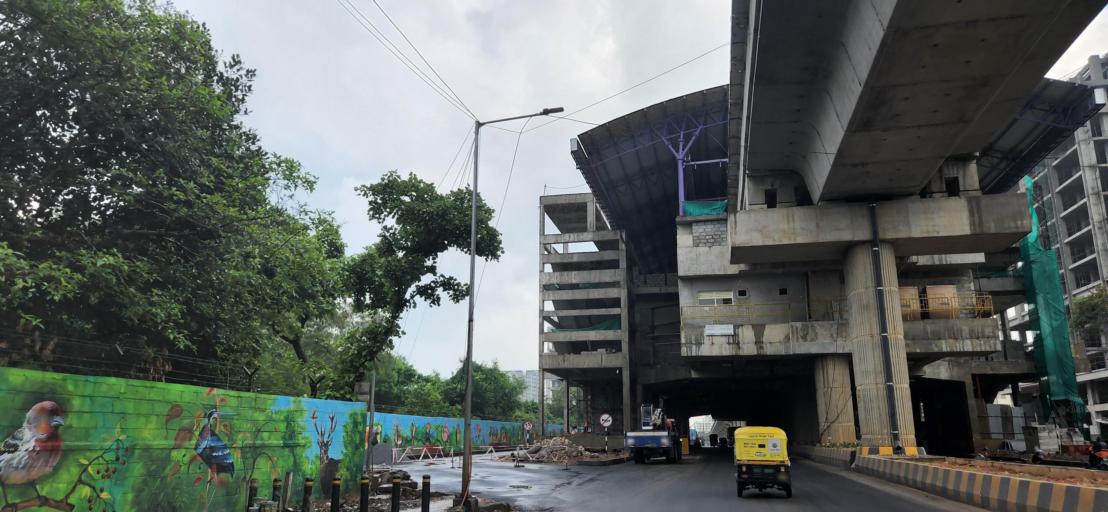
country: IN
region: Karnataka
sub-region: Bangalore Rural
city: Hoskote
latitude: 12.9865
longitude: 77.7442
